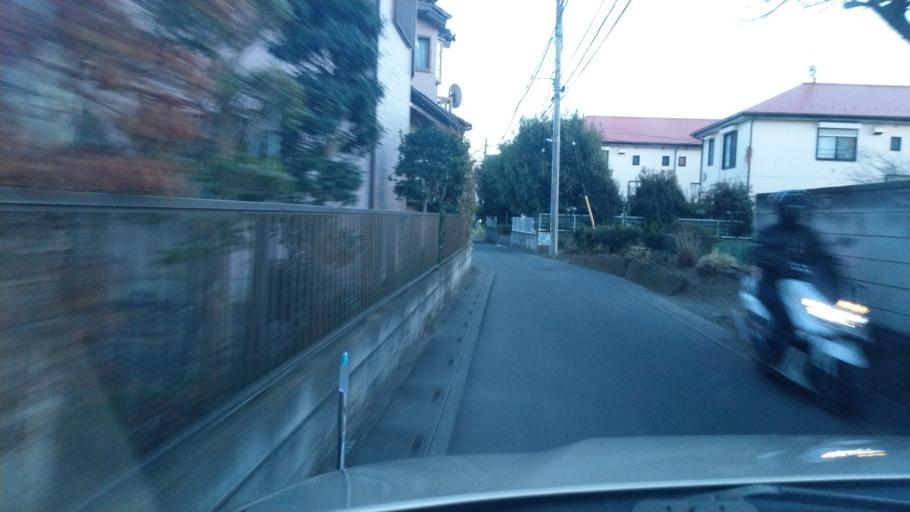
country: JP
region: Saitama
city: Yono
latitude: 35.9138
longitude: 139.5850
